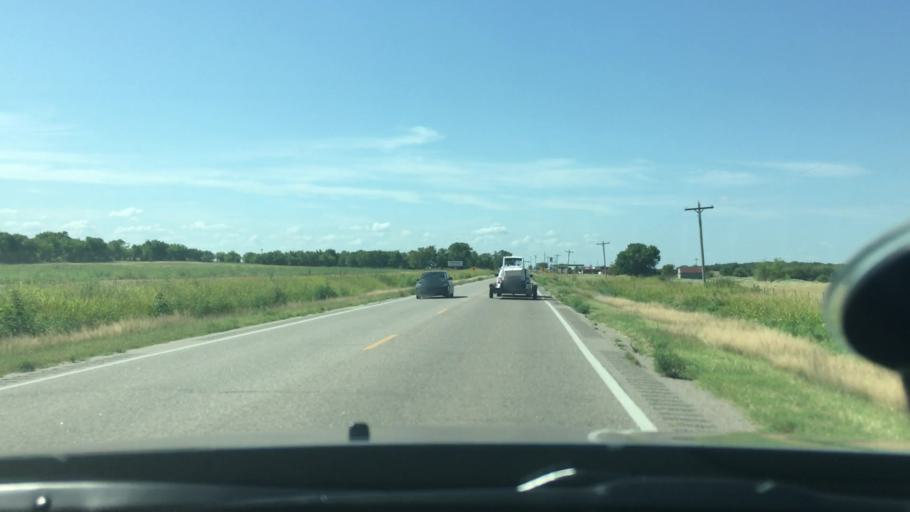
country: US
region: Oklahoma
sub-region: Marshall County
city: Kingston
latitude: 34.0030
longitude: -96.7611
